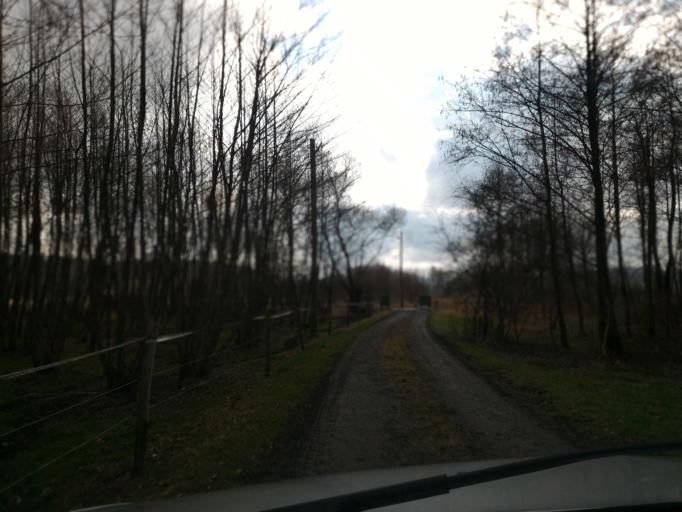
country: CZ
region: Liberecky
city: Visnova
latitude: 50.9904
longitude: 15.0243
